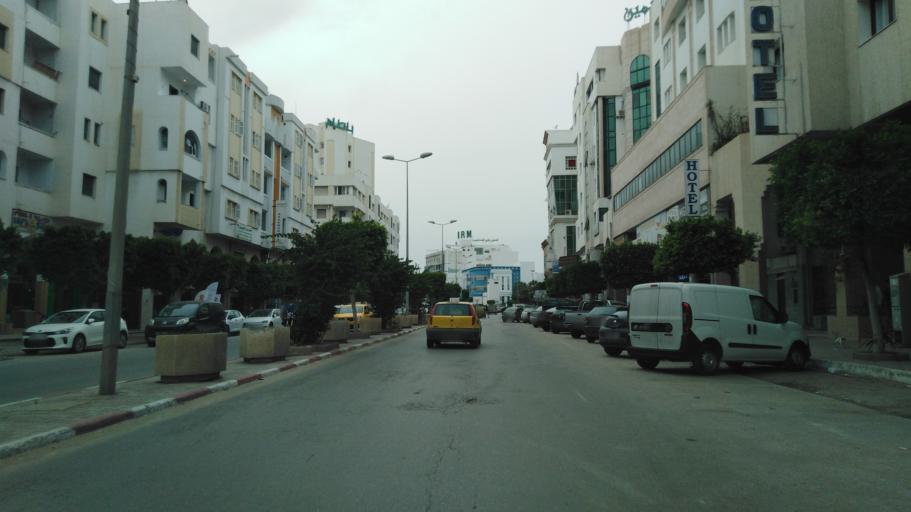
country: TN
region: Safaqis
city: Sfax
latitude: 34.7398
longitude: 10.7536
